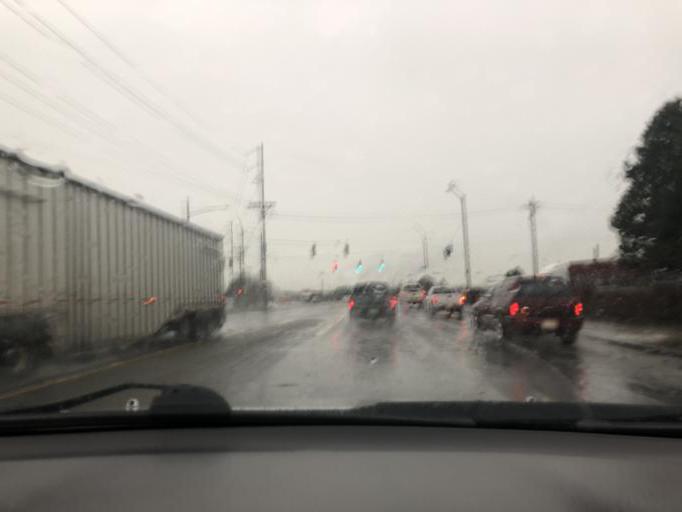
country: US
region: Washington
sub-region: Pierce County
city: Tacoma
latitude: 47.2483
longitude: -122.4151
